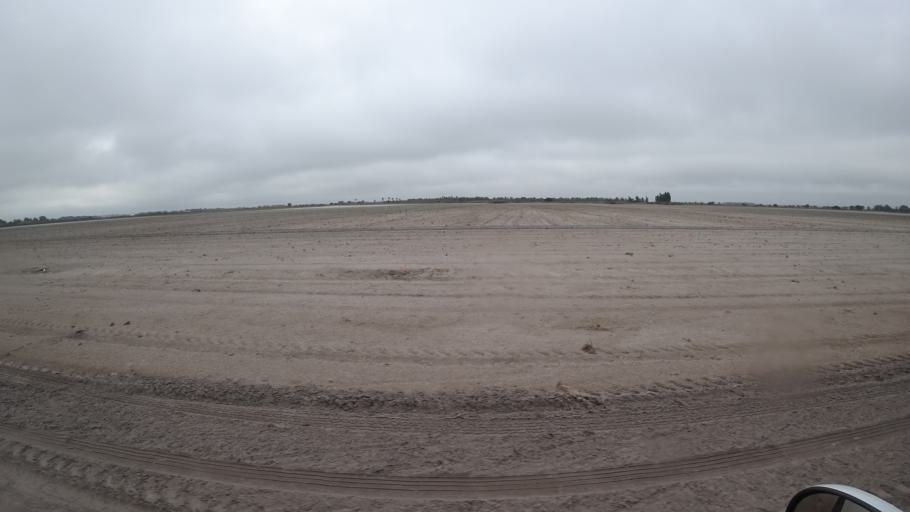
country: US
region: Florida
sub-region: Sarasota County
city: Warm Mineral Springs
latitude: 27.2898
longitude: -82.1753
